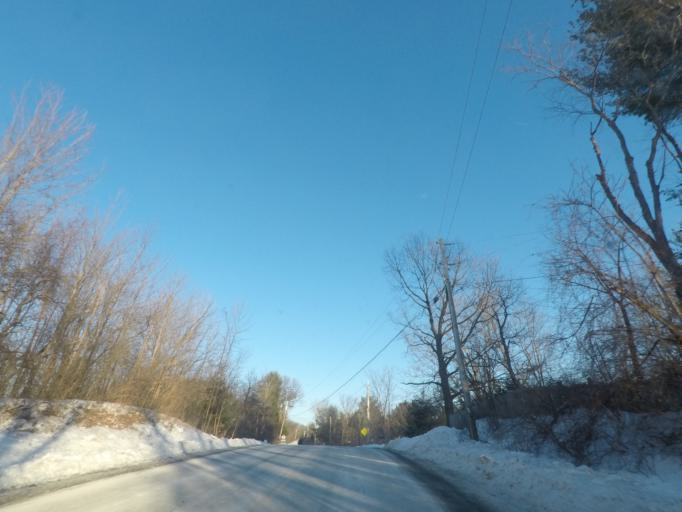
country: US
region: New York
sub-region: Saratoga County
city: Waterford
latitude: 42.8329
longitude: -73.6596
